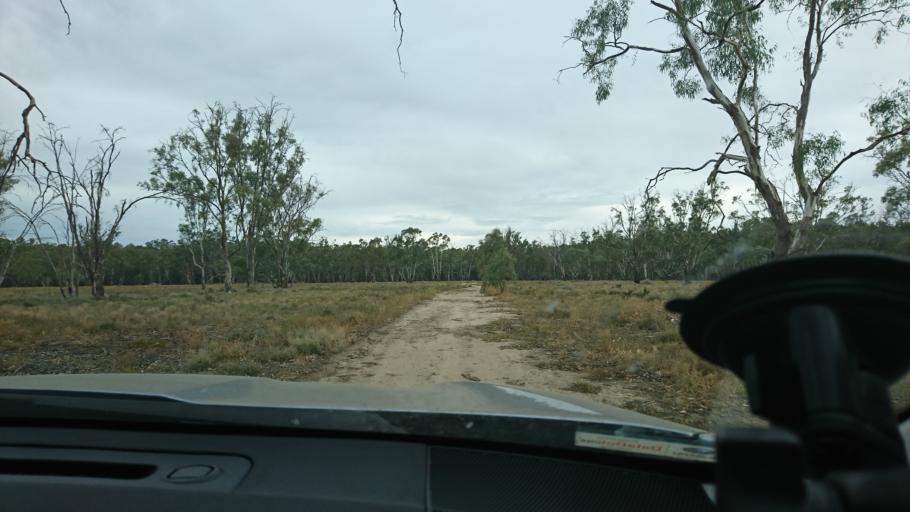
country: AU
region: Victoria
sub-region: Swan Hill
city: Swan Hill
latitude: -35.1399
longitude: 143.3798
